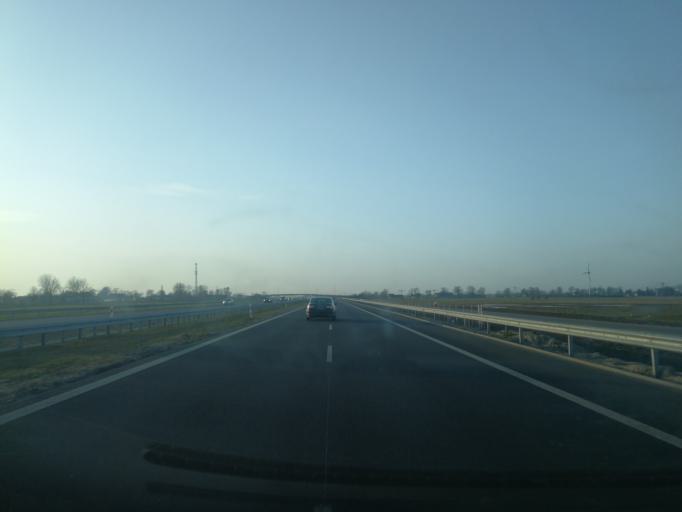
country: PL
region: Pomeranian Voivodeship
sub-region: Powiat nowodworski
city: Ostaszewo
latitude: 54.2467
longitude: 18.9938
